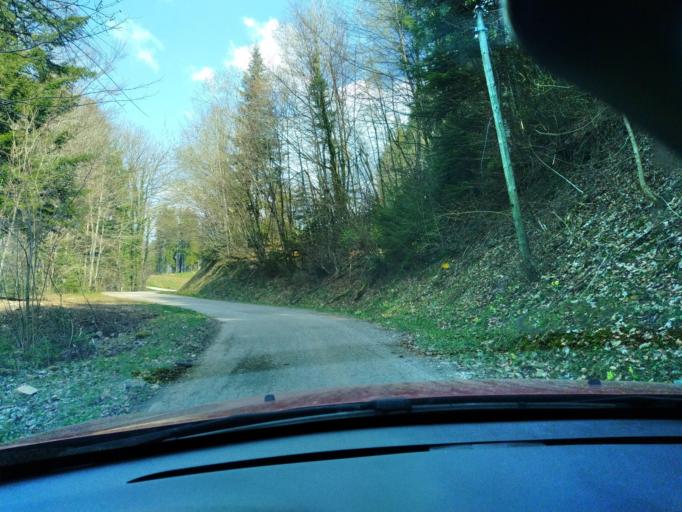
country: FR
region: Franche-Comte
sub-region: Departement du Jura
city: Lavans-les-Saint-Claude
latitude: 46.3980
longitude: 5.7482
